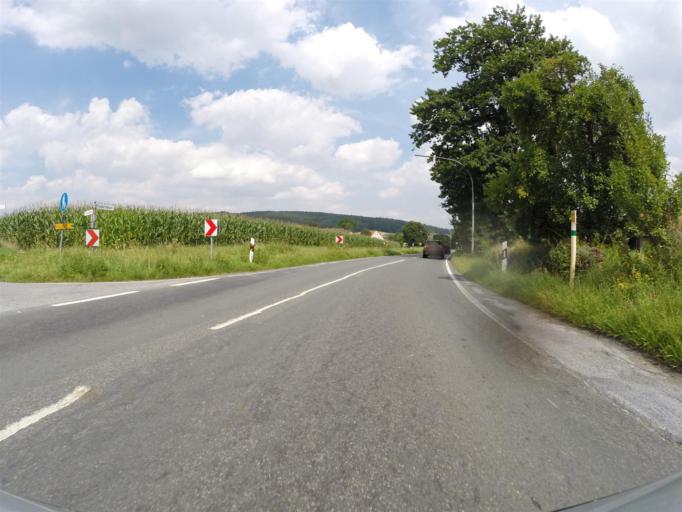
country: DE
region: North Rhine-Westphalia
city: Preussisch Oldendorf
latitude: 52.2739
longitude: 8.5163
